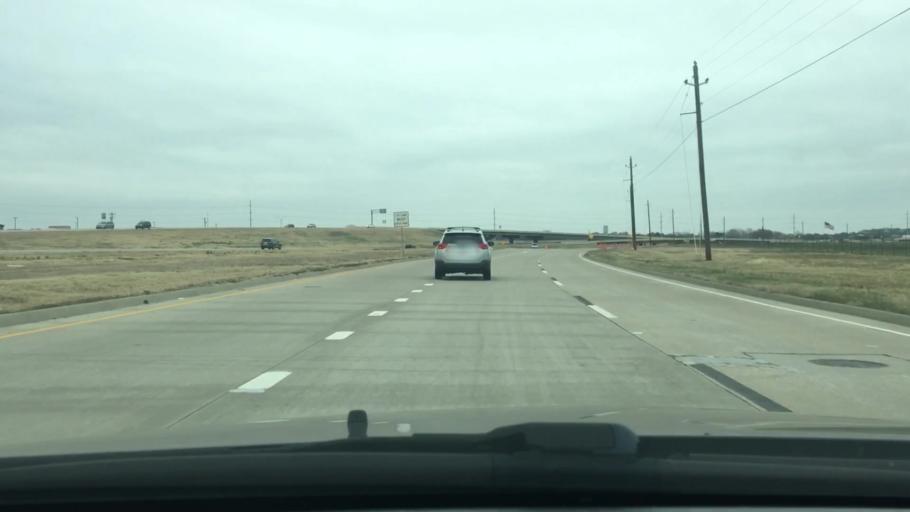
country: US
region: Texas
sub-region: Denton County
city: Roanoke
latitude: 32.9961
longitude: -97.2181
